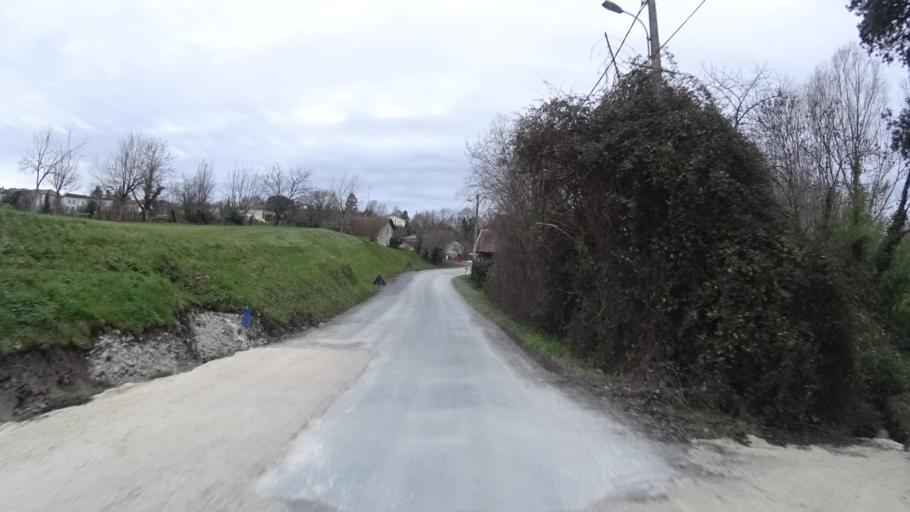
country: FR
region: Aquitaine
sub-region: Departement de la Dordogne
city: Saint-Aulaye
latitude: 45.2060
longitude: 0.1362
